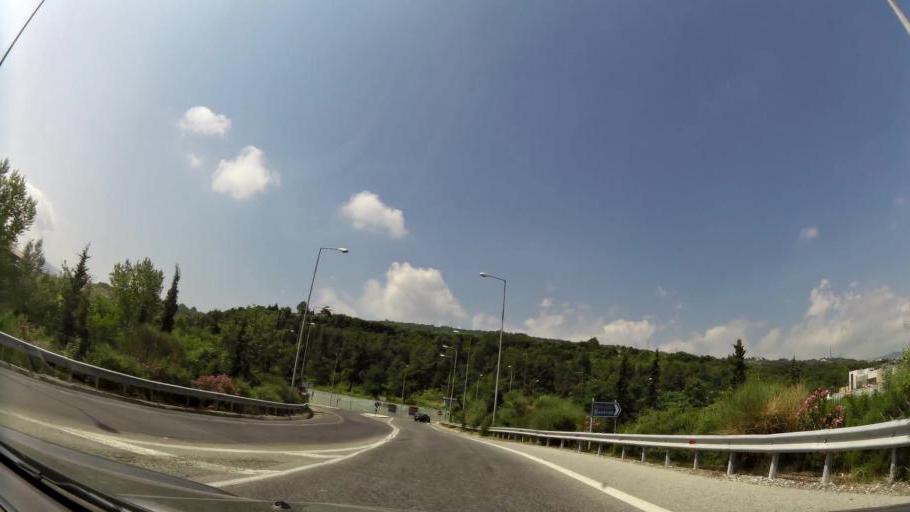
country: GR
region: Central Macedonia
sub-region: Nomos Imathias
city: Veroia
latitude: 40.5067
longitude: 22.2284
